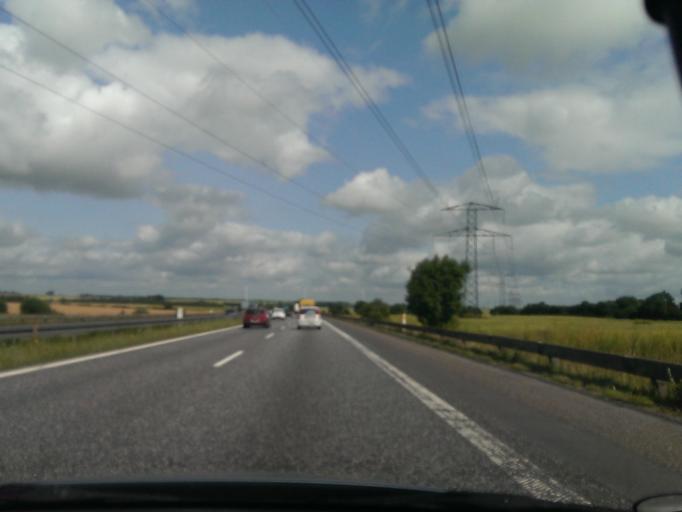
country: DK
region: Central Jutland
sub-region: Randers Kommune
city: Spentrup
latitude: 56.5026
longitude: 9.9765
